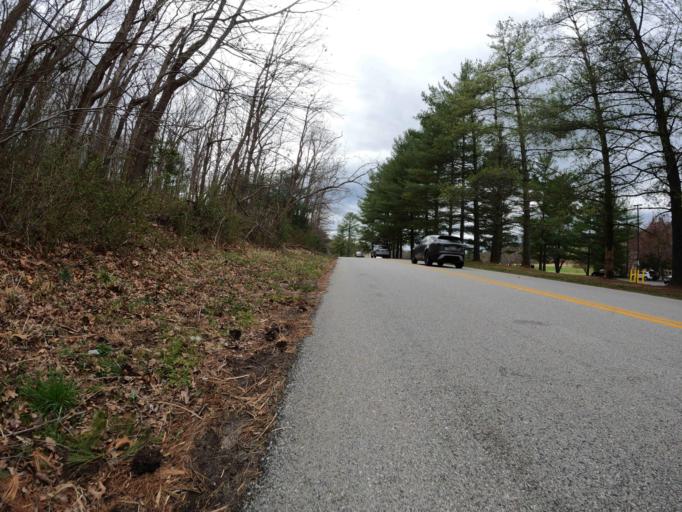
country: US
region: Maryland
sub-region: Howard County
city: Columbia
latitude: 39.2958
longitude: -76.8839
